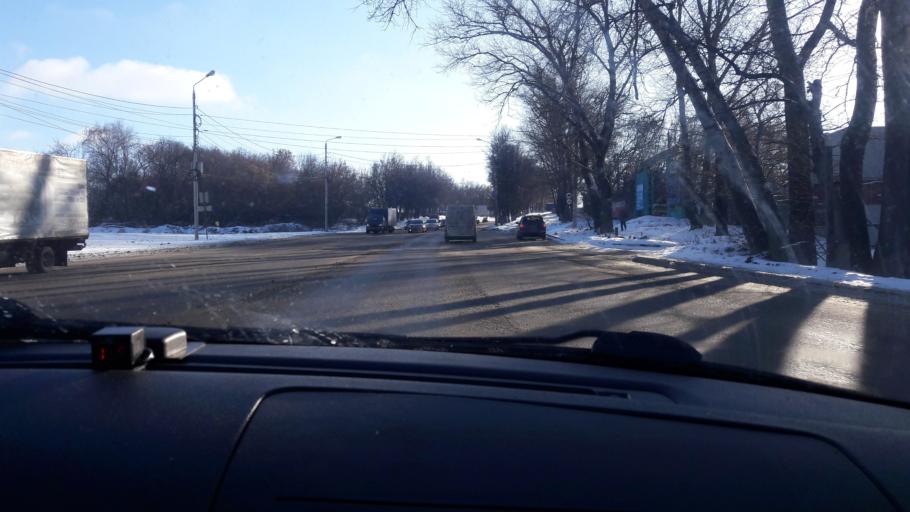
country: RU
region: Tula
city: Tula
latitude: 54.1702
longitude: 37.6392
